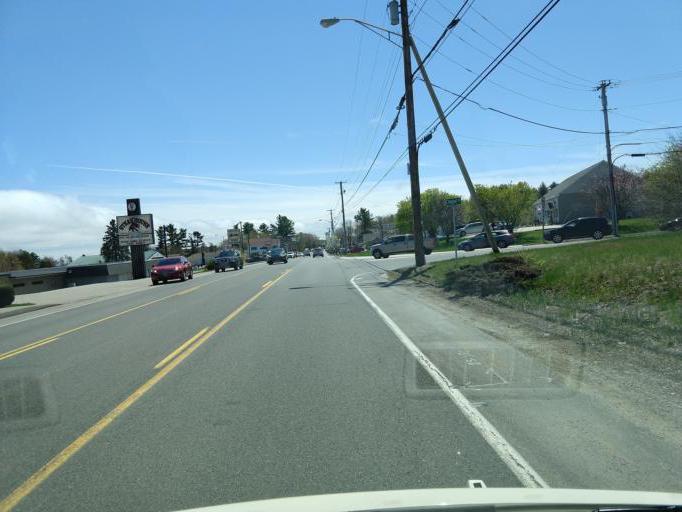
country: US
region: Maine
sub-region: York County
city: Wells Beach Station
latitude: 43.3105
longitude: -70.5848
